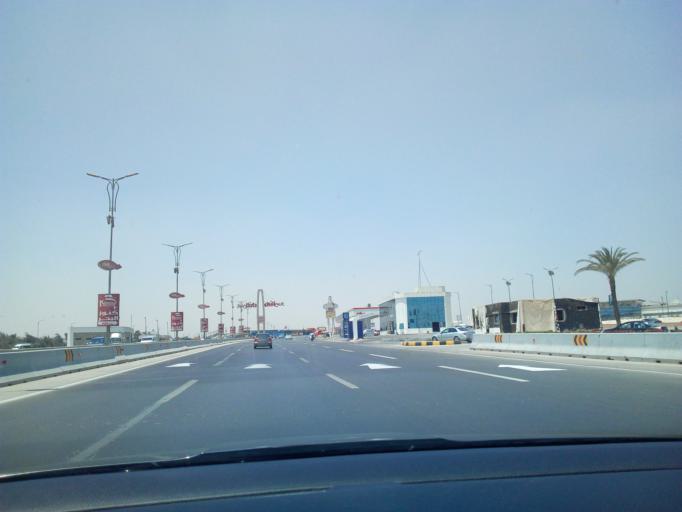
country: EG
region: Al Jizah
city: Awsim
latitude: 30.0656
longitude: 31.0210
